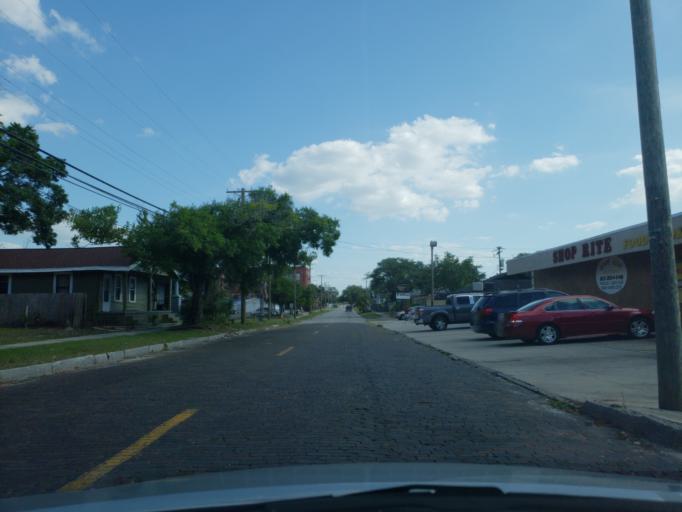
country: US
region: Florida
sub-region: Hillsborough County
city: Tampa
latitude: 27.9637
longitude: -82.4808
